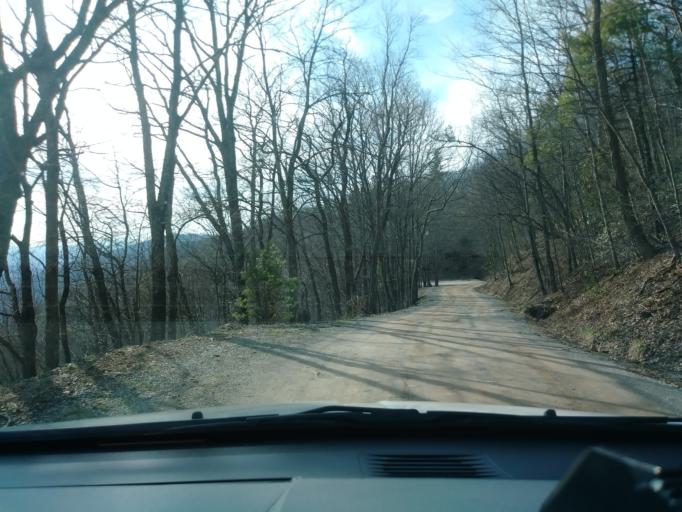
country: US
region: Tennessee
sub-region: Greene County
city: Tusculum
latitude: 36.0326
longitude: -82.7237
